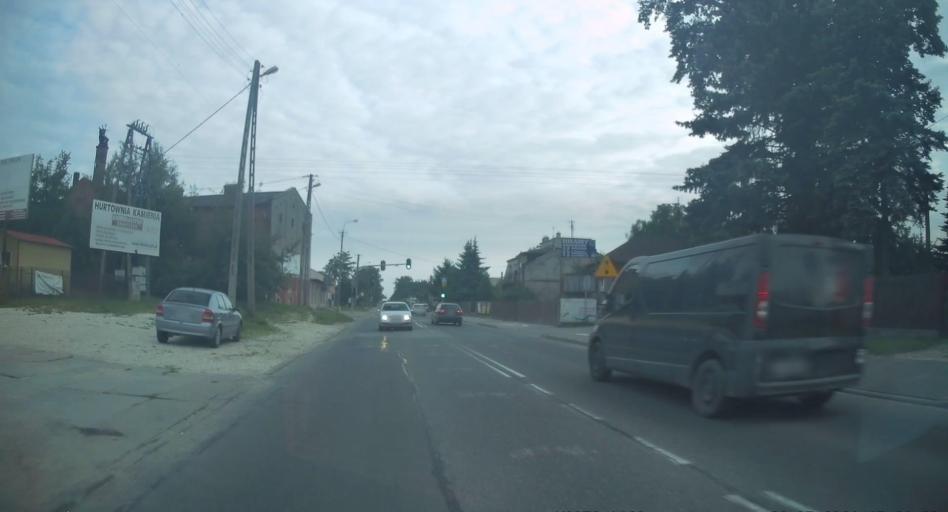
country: PL
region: Lodz Voivodeship
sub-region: Powiat radomszczanski
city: Radomsko
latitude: 51.0470
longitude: 19.4387
